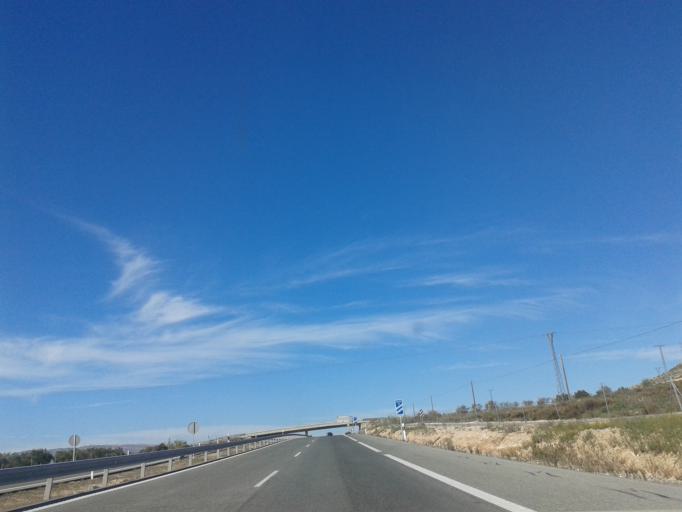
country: ES
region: Valencia
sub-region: Provincia de Alicante
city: Villena
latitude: 38.6937
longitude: -0.9129
